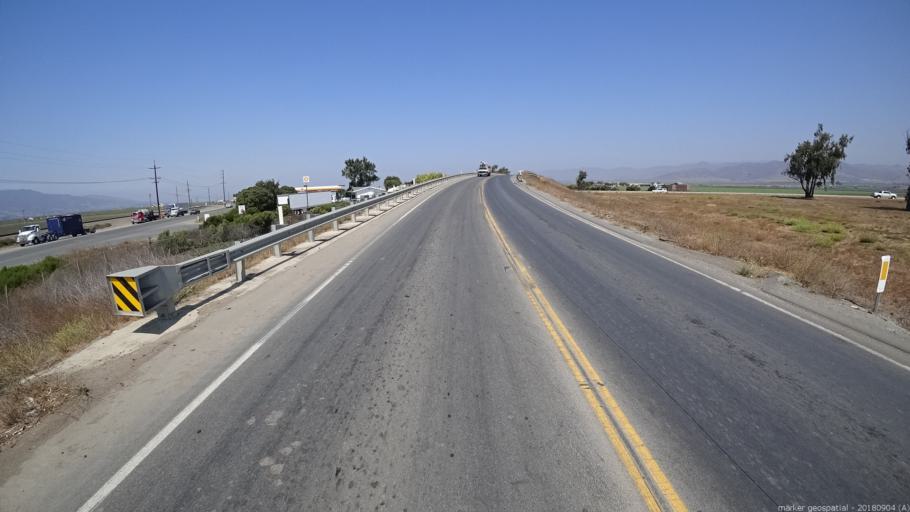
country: US
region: California
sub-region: Monterey County
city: Gonzales
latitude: 36.5224
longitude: -121.4639
